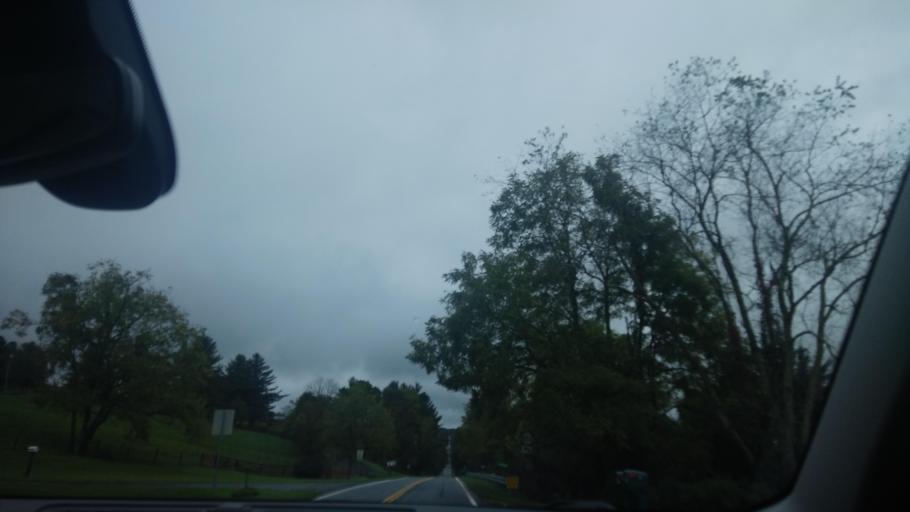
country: US
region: Virginia
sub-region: City of Galax
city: Galax
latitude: 36.6255
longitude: -80.9211
